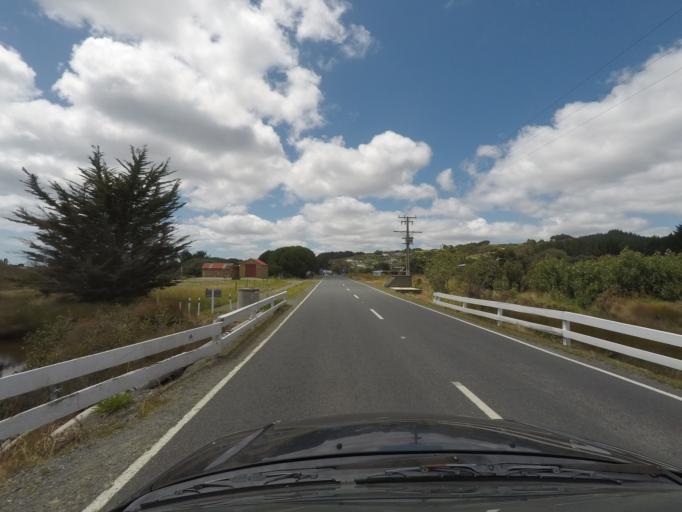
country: NZ
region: Northland
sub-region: Whangarei
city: Ruakaka
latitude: -36.0252
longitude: 174.5005
